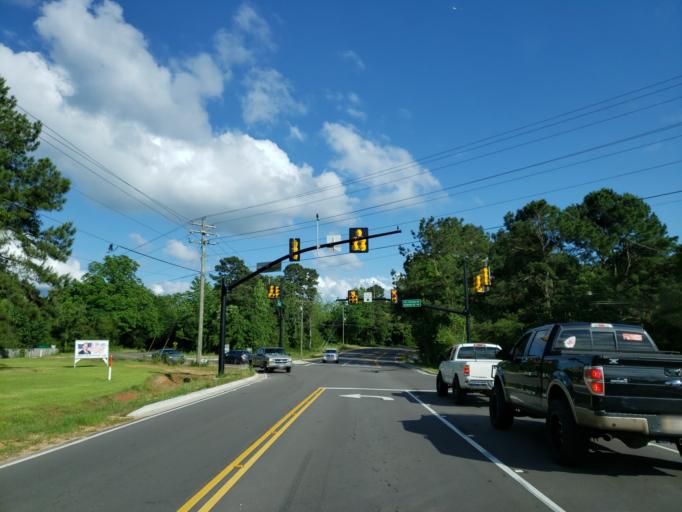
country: US
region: Mississippi
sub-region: Lamar County
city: West Hattiesburg
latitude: 31.2714
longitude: -89.4125
